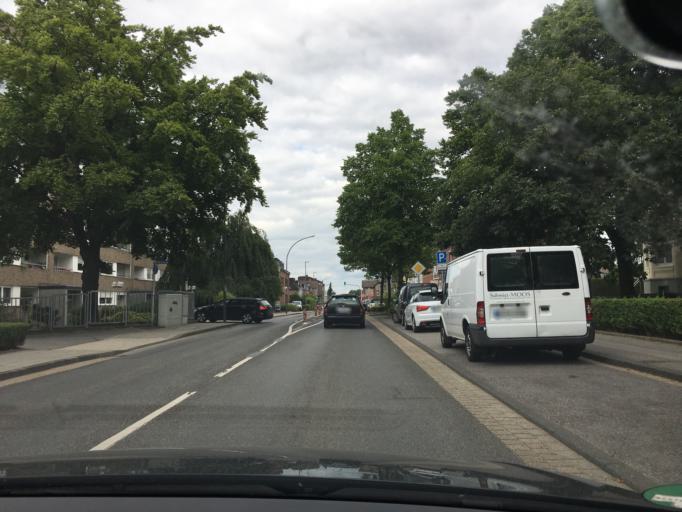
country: DE
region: North Rhine-Westphalia
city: Stolberg
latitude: 50.7498
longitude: 6.1671
